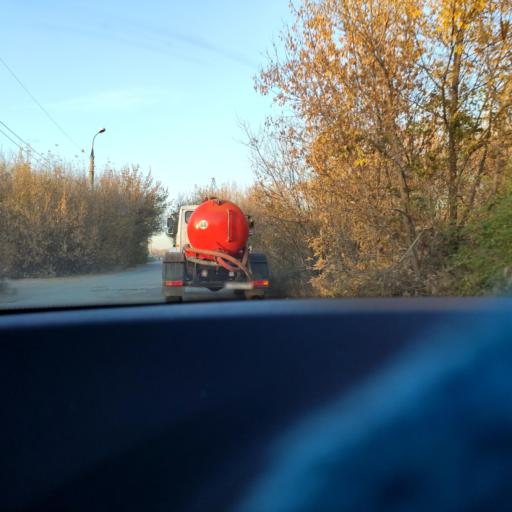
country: RU
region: Samara
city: Petra-Dubrava
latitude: 53.2599
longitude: 50.2976
